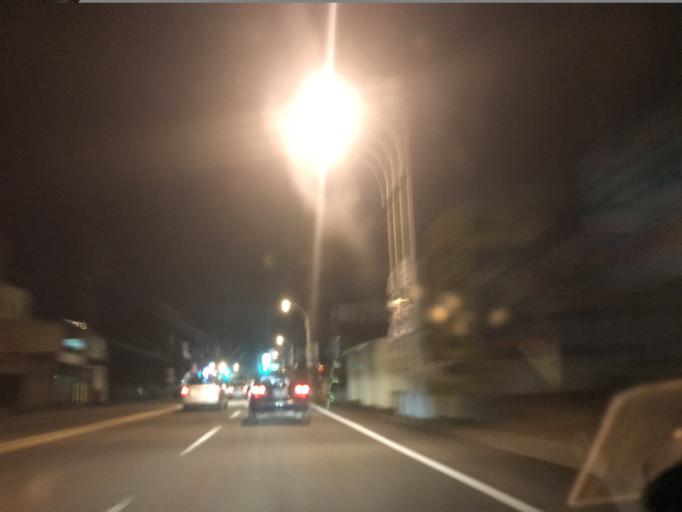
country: TW
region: Taiwan
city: Daxi
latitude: 24.8366
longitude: 121.2079
